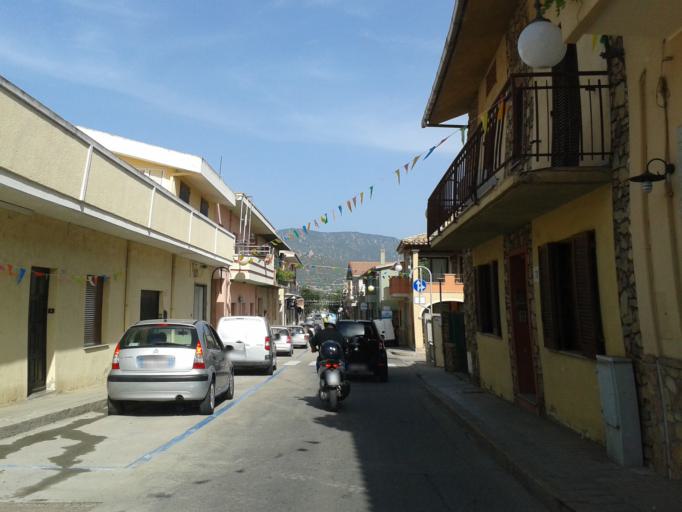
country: IT
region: Sardinia
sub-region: Provincia di Cagliari
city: Villasimius
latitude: 39.1452
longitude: 9.5175
